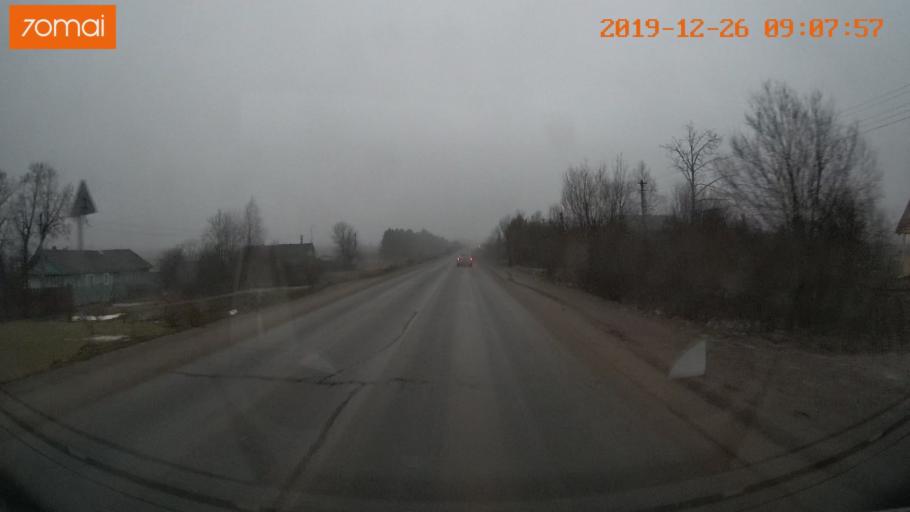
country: RU
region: Vologda
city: Gryazovets
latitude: 58.8515
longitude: 40.2471
